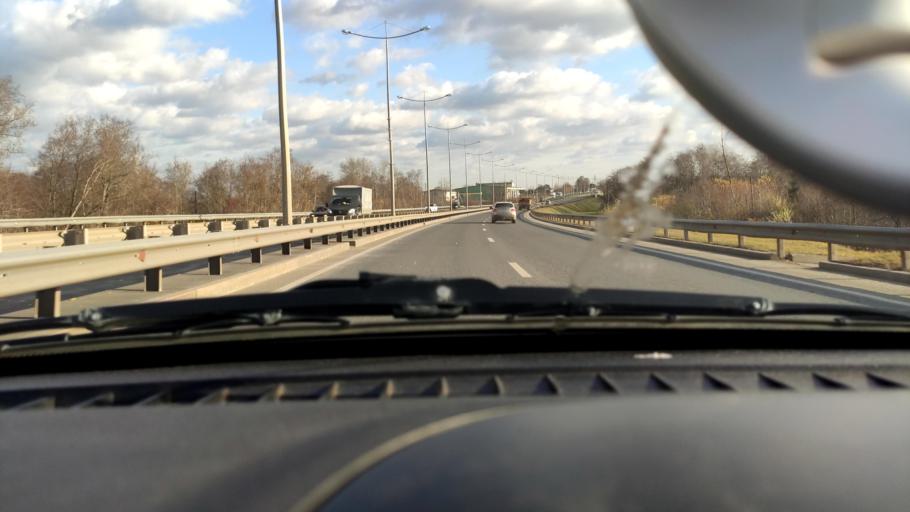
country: RU
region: Perm
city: Kondratovo
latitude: 57.9347
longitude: 56.0270
